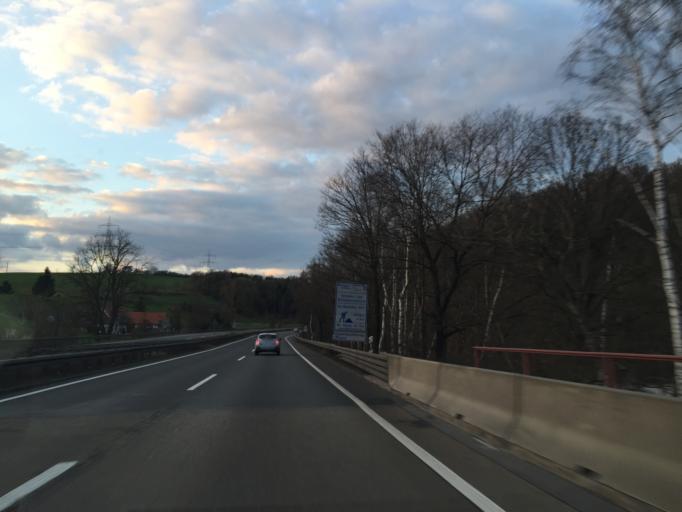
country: DE
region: Hesse
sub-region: Regierungsbezirk Kassel
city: Bad Hersfeld
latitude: 50.8689
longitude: 9.7866
